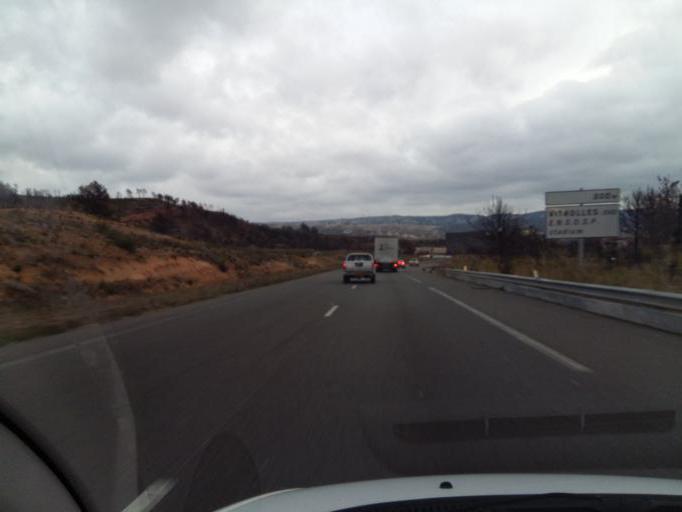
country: FR
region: Provence-Alpes-Cote d'Azur
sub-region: Departement des Bouches-du-Rhone
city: Les Pennes-Mirabeau
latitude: 43.4474
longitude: 5.2979
